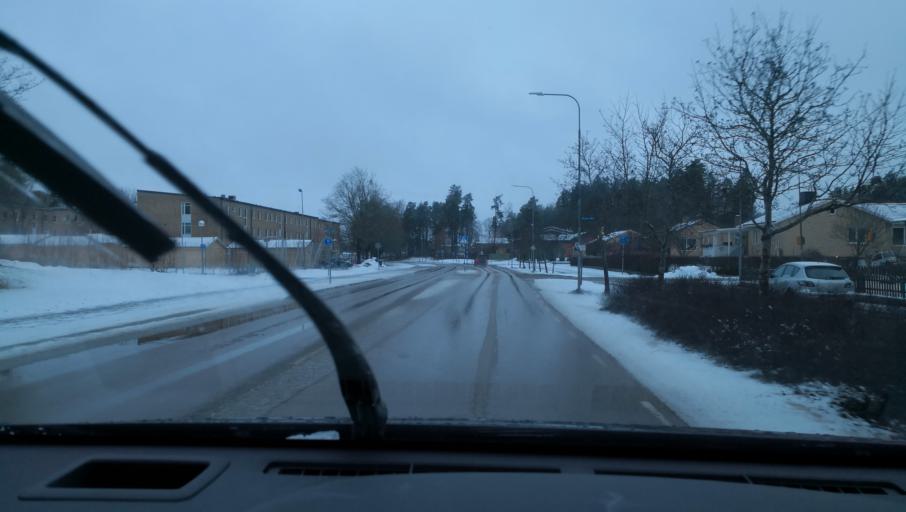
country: SE
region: Vaestmanland
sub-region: Kopings Kommun
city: Koping
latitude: 59.5217
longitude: 16.0035
